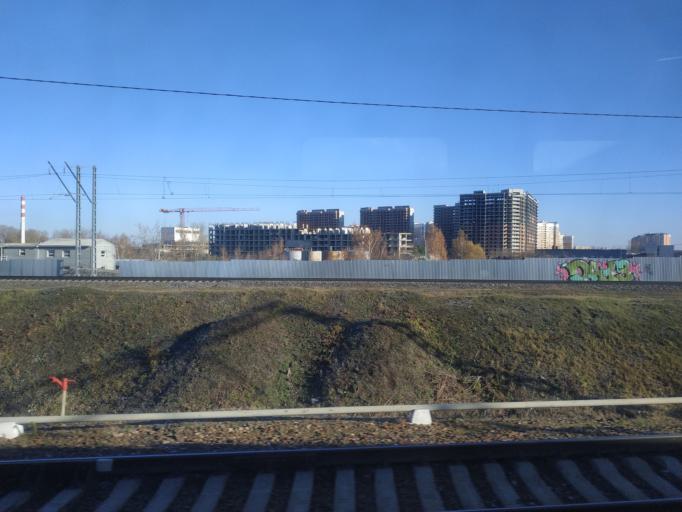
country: RU
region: Moskovskaya
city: Biryulevo Zapadnoye
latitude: 55.6028
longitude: 37.6476
